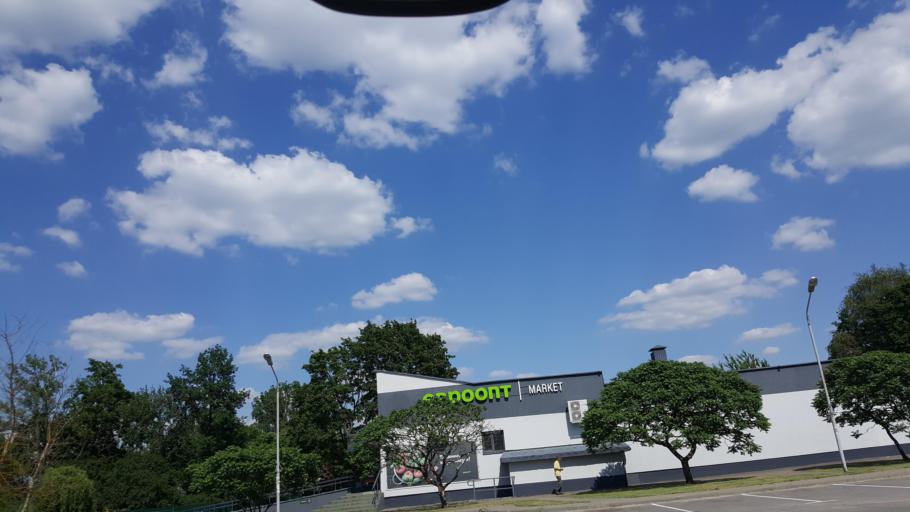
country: BY
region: Brest
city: Horad Kobryn
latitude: 52.2128
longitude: 24.3760
